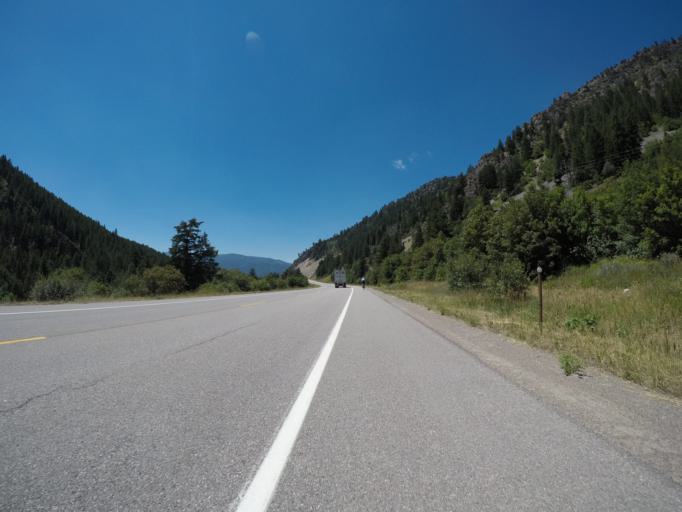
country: US
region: Wyoming
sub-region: Teton County
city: Hoback
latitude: 43.1777
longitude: -110.9899
